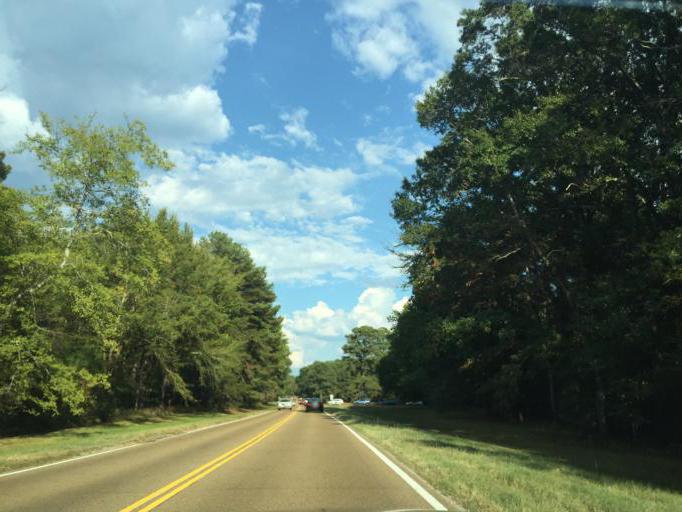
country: US
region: Mississippi
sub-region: Madison County
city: Ridgeland
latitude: 32.4263
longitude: -90.1283
